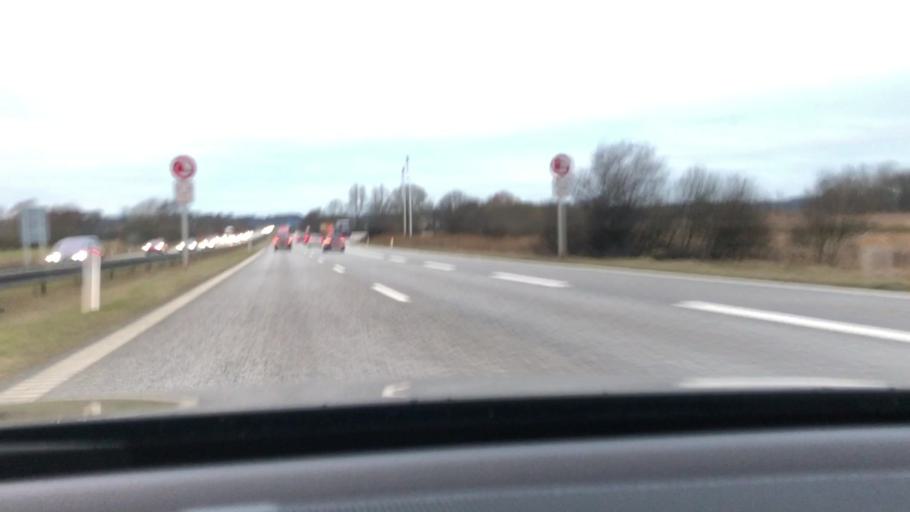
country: DK
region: Central Jutland
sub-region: Randers Kommune
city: Randers
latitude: 56.4471
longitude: 10.0038
